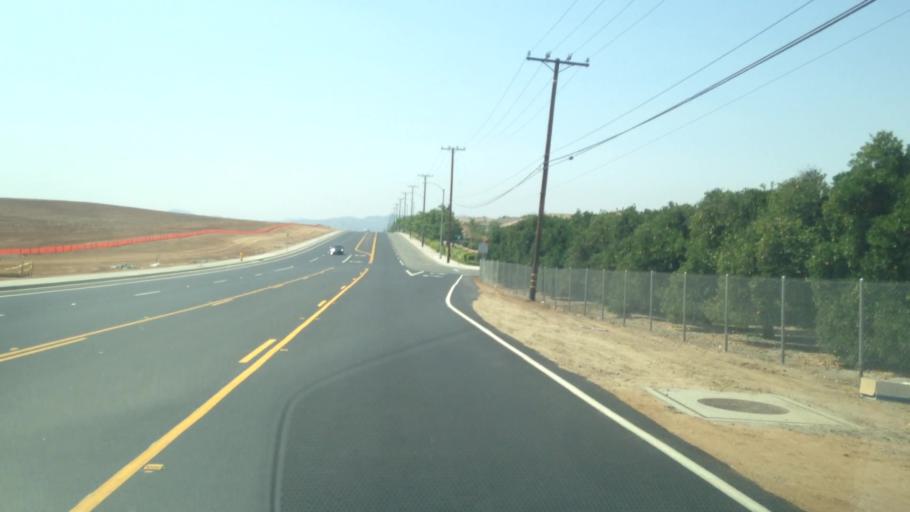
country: US
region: California
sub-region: Riverside County
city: Woodcrest
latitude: 33.8858
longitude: -117.3139
